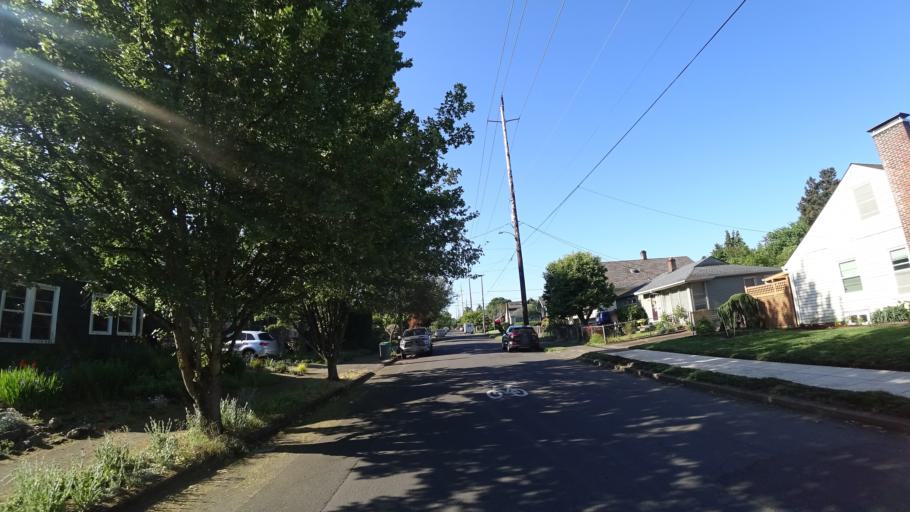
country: US
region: Oregon
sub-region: Multnomah County
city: Portland
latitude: 45.5750
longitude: -122.6668
